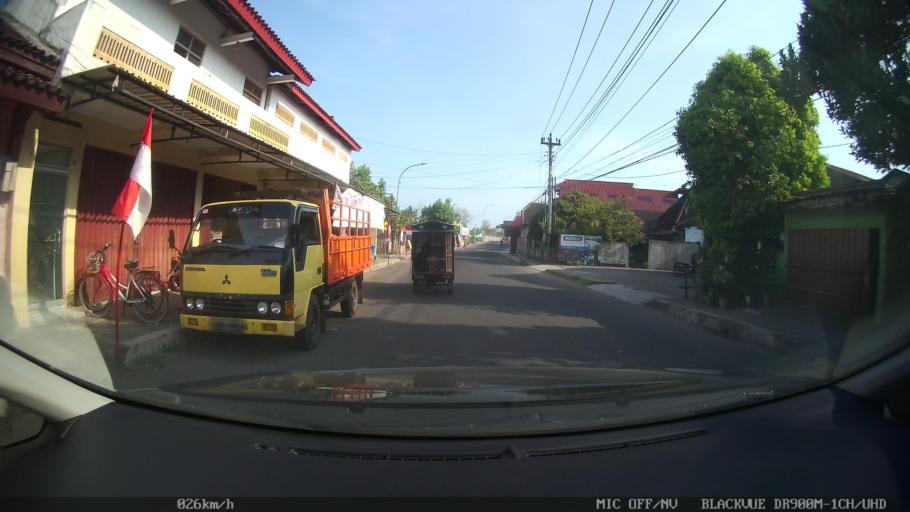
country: ID
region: Daerah Istimewa Yogyakarta
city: Pandak
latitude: -7.8976
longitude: 110.2982
